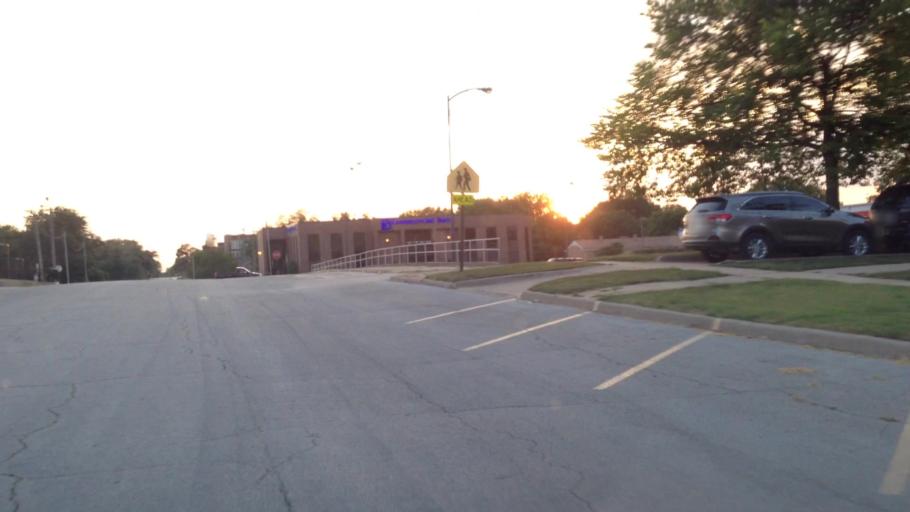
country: US
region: Kansas
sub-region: Montgomery County
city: Independence
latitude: 37.2277
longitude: -95.7053
